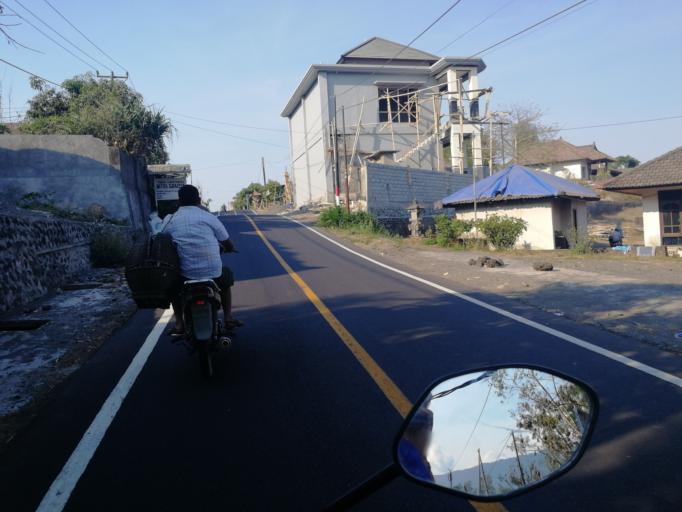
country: ID
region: Bali
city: Banjar Trunyan
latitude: -8.2469
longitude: 115.3999
